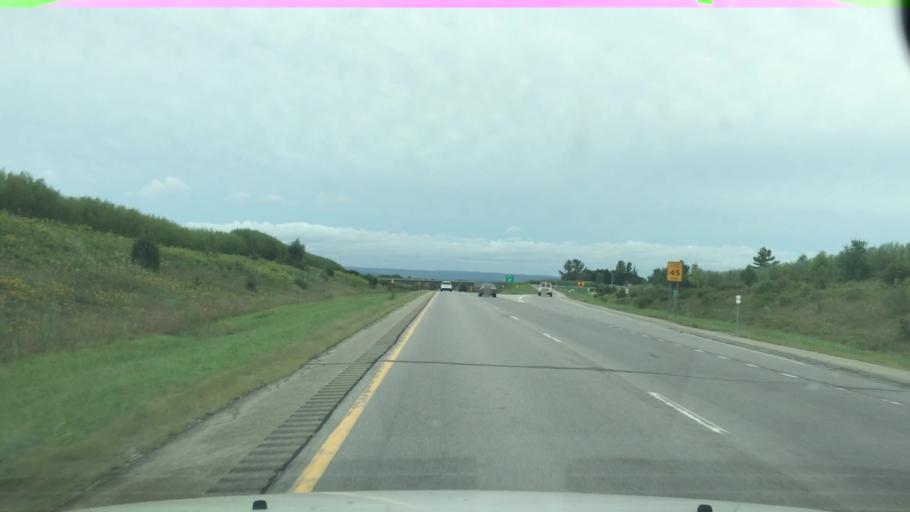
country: US
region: New York
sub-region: Erie County
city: Springville
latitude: 42.5572
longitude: -78.7120
